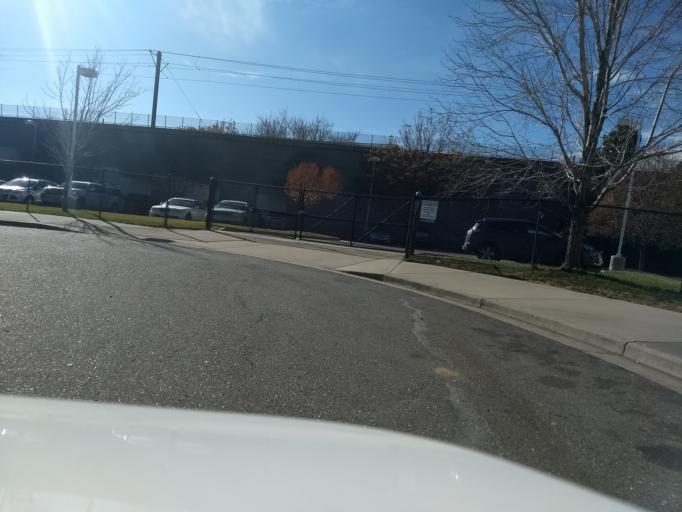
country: US
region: Colorado
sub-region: Denver County
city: Denver
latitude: 39.7174
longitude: -104.9976
